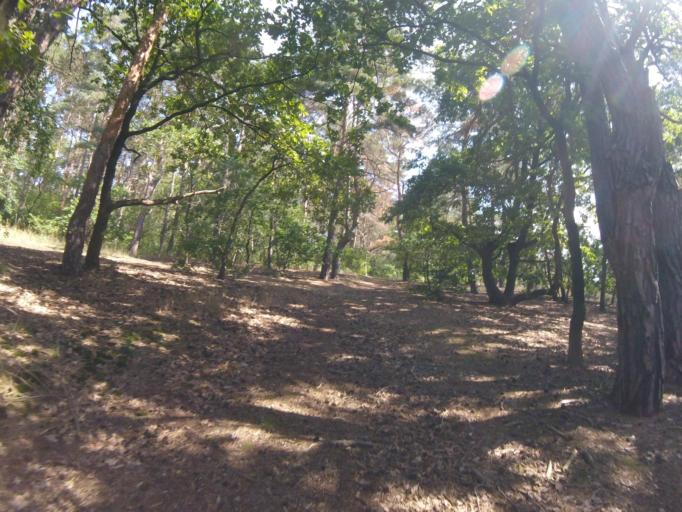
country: DE
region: Brandenburg
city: Wildau
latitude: 52.3230
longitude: 13.6084
